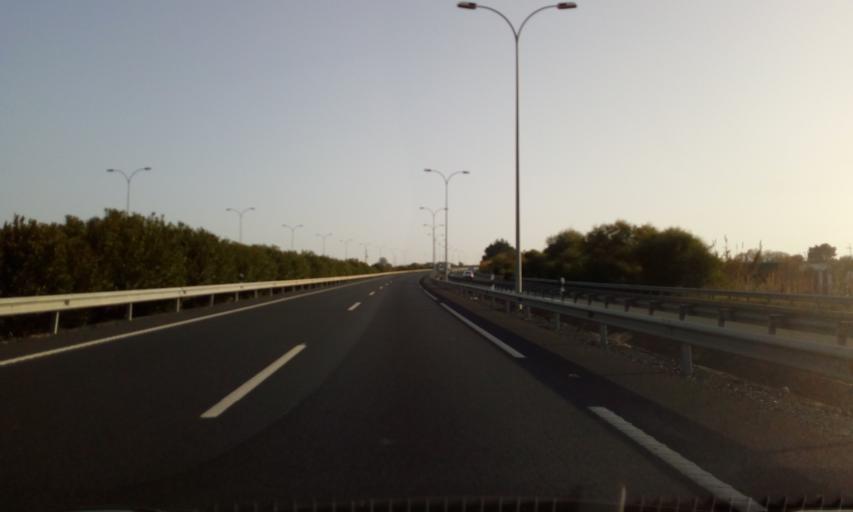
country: ES
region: Andalusia
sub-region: Provincia de Huelva
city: Bollullos par del Condado
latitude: 37.3563
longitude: -6.5513
